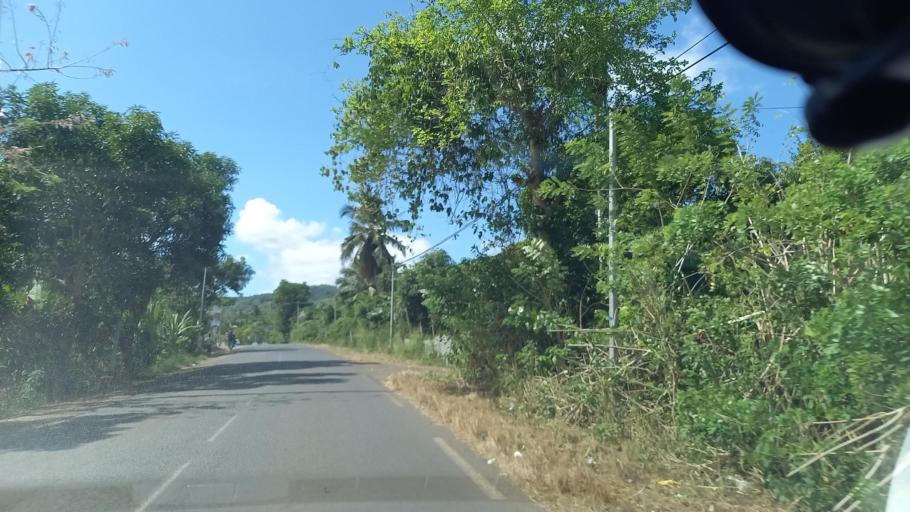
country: YT
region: Chirongui
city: Chirongui
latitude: -12.9241
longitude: 45.1563
